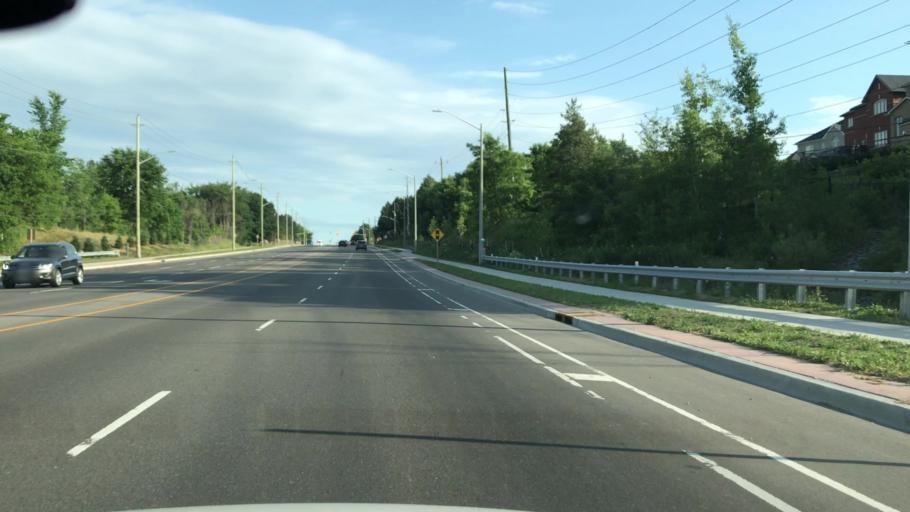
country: CA
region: Ontario
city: Newmarket
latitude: 44.0468
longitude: -79.4274
